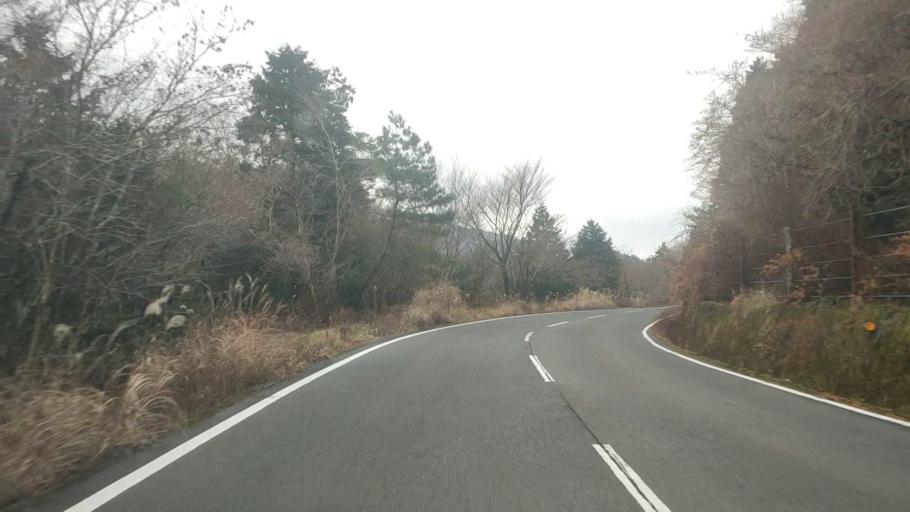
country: JP
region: Nagasaki
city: Shimabara
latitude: 32.7700
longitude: 130.2716
